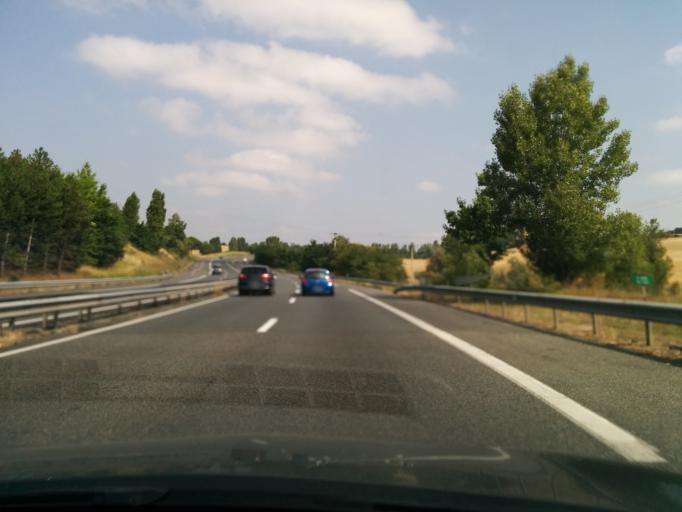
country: FR
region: Midi-Pyrenees
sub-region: Departement de la Haute-Garonne
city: Garidech
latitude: 43.7084
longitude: 1.5688
